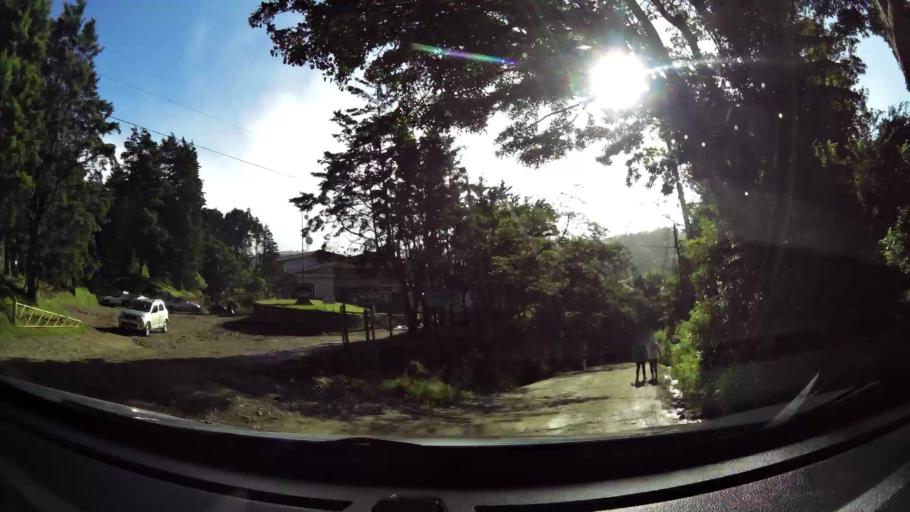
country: CR
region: Guanacaste
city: Juntas
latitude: 10.3051
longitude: -84.8096
